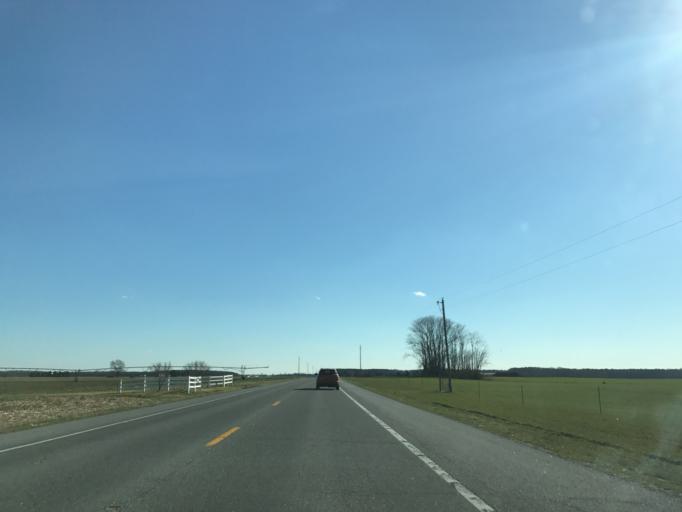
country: US
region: Maryland
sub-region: Caroline County
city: Greensboro
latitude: 39.1253
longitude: -75.8670
